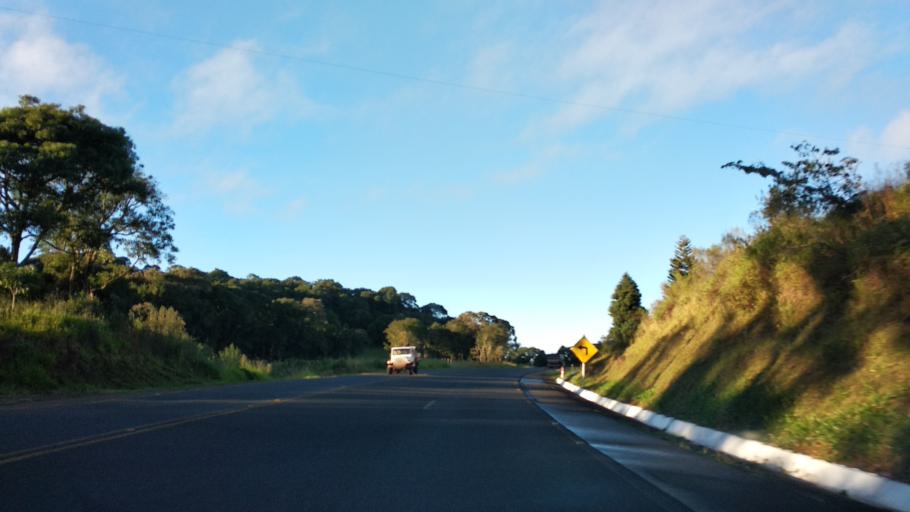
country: BR
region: Santa Catarina
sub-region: Curitibanos
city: Curitibanos
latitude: -27.6100
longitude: -50.7178
